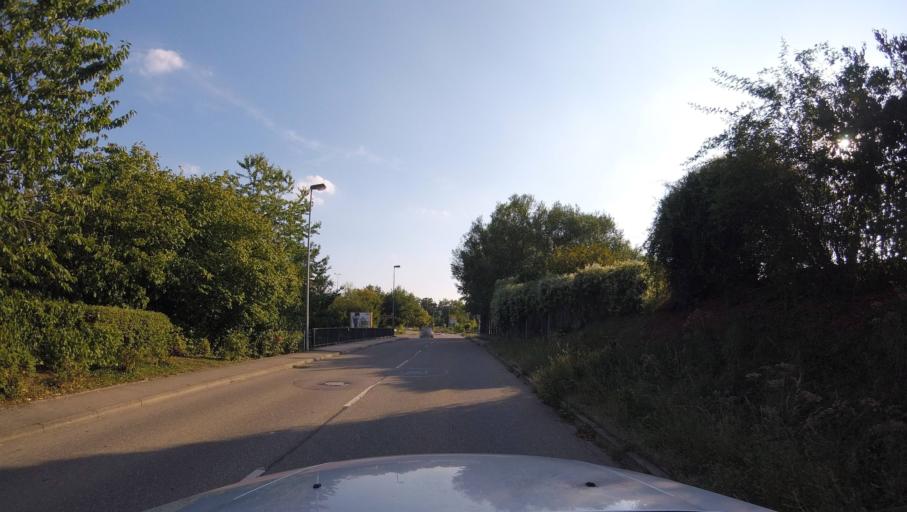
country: DE
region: Baden-Wuerttemberg
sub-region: Regierungsbezirk Stuttgart
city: Rudersberg
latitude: 48.8853
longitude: 9.5338
